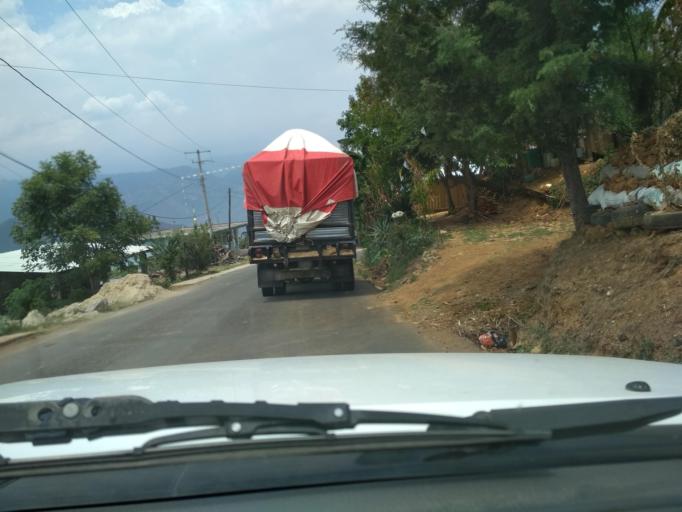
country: MX
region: Veracruz
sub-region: Acultzingo
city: Acatla
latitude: 18.7521
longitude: -97.1953
